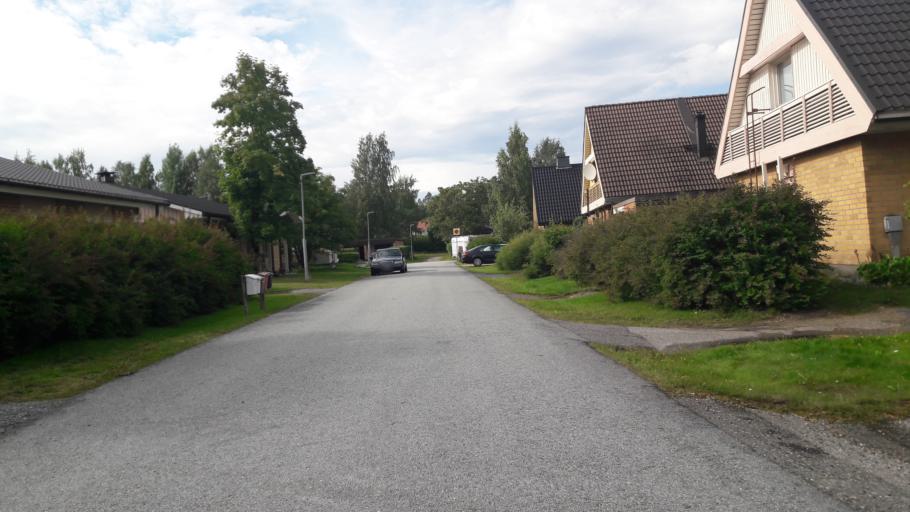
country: FI
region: North Karelia
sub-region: Joensuu
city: Joensuu
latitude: 62.5806
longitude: 29.8099
